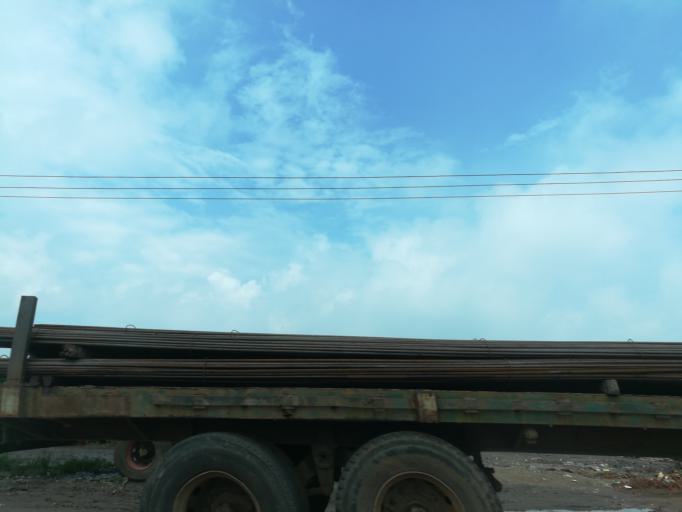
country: NG
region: Lagos
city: Ikorodu
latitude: 6.6683
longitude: 3.5140
